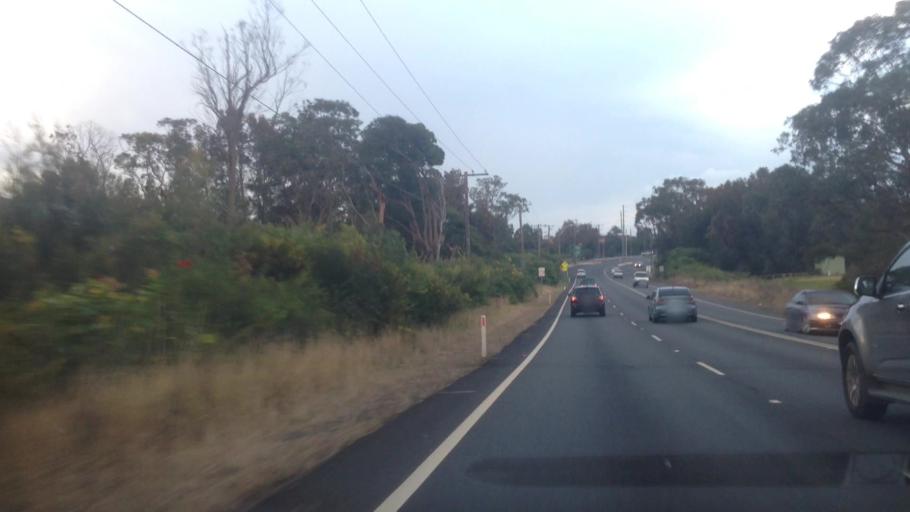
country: AU
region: New South Wales
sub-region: Wyong Shire
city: Kanwal
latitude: -33.2551
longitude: 151.4872
